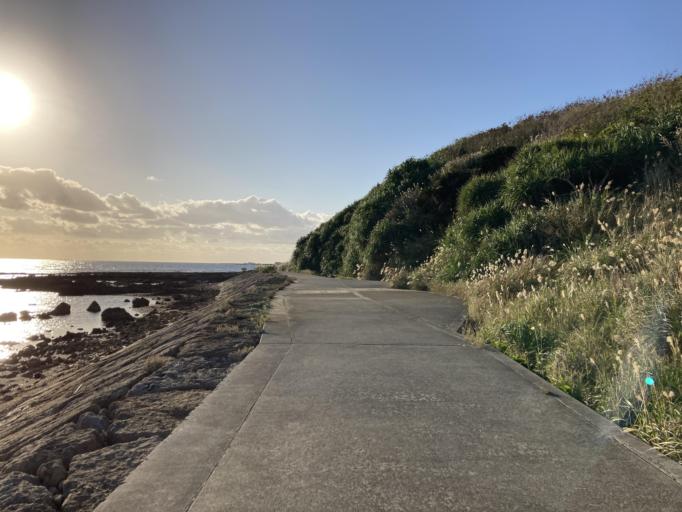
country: JP
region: Okinawa
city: Ginowan
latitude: 26.1893
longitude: 127.8219
